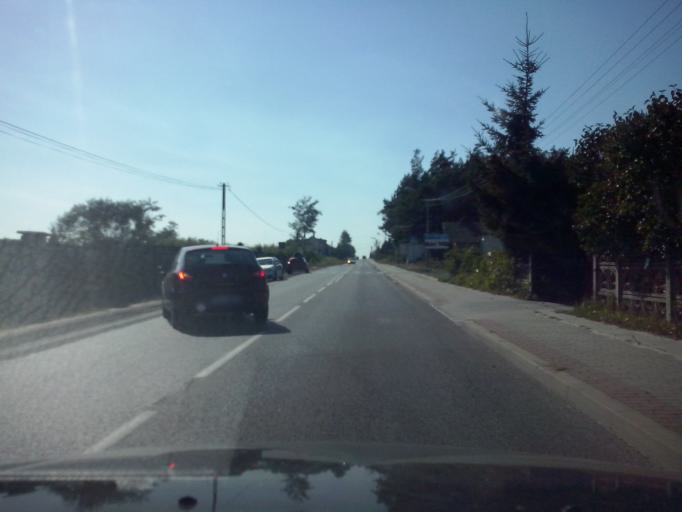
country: PL
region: Swietokrzyskie
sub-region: Powiat kielecki
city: Domaszowice
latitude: 50.8141
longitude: 20.6959
